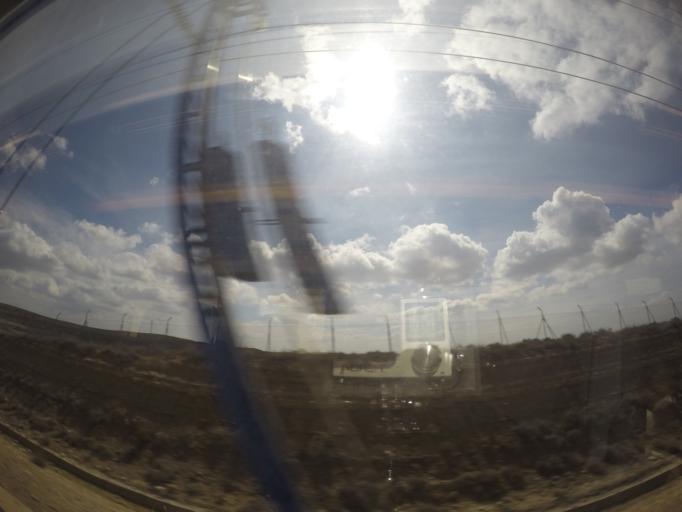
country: ES
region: Aragon
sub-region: Provincia de Huesca
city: Candasnos
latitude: 41.5621
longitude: 0.0836
